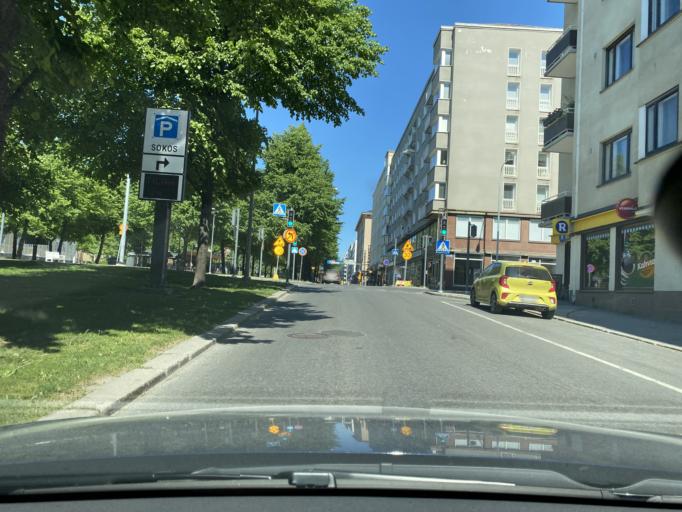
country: FI
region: Pirkanmaa
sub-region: Tampere
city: Tampere
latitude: 61.4959
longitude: 23.7529
